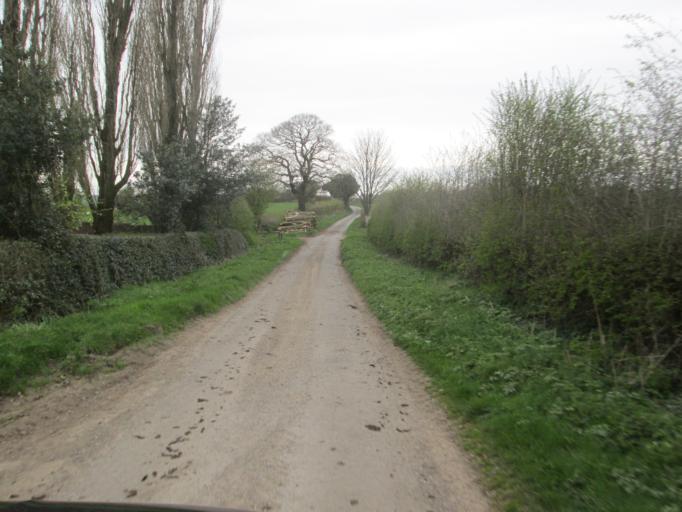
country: GB
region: England
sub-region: Derbyshire
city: Duffield
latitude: 52.9818
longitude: -1.5273
